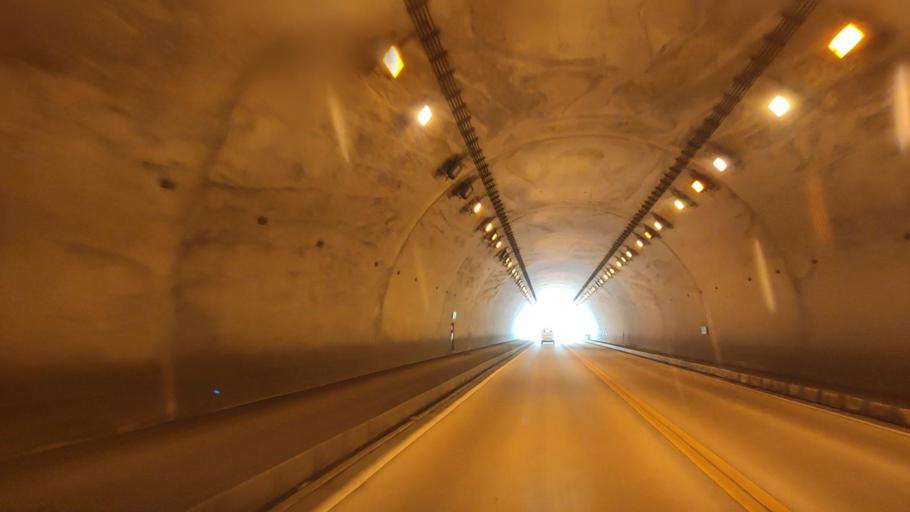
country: JP
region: Hyogo
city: Toyooka
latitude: 35.4635
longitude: 134.7682
